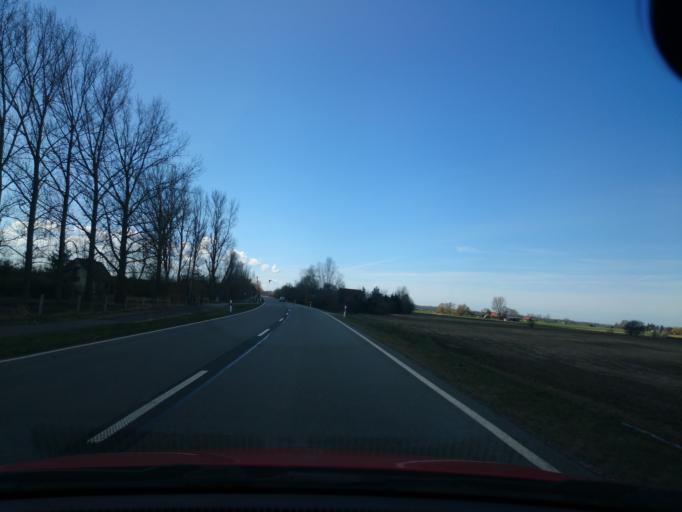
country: DE
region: Mecklenburg-Vorpommern
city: Trinwillershagen
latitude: 54.2875
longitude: 12.6278
